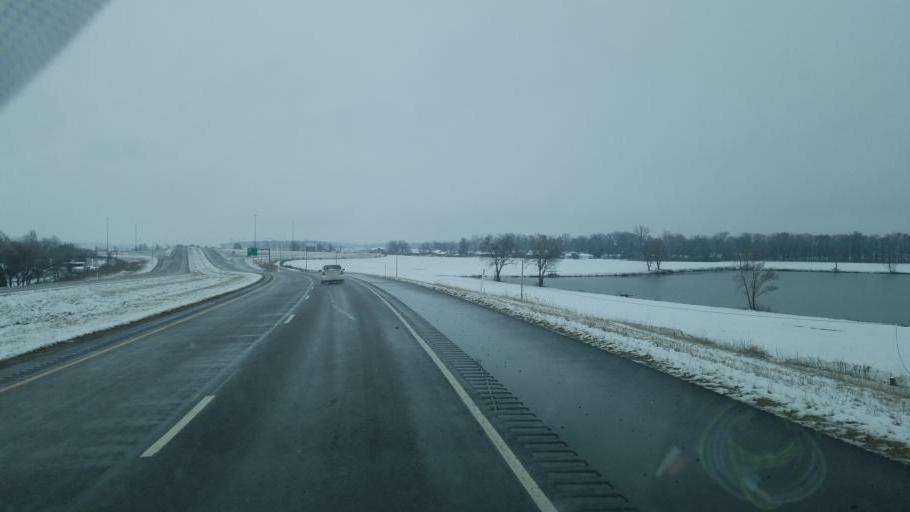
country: US
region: Indiana
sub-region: Delaware County
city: Muncie
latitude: 40.2435
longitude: -85.3655
